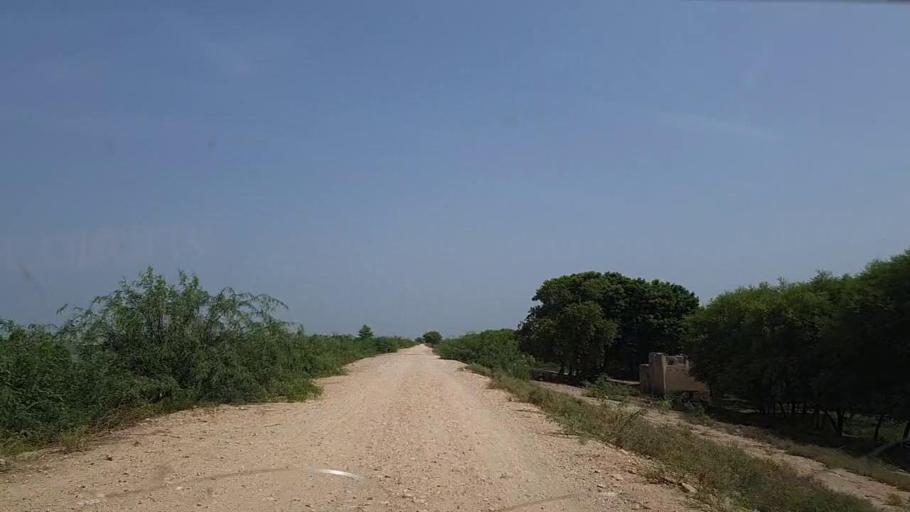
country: PK
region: Sindh
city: Ghotki
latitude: 28.0975
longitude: 69.4035
